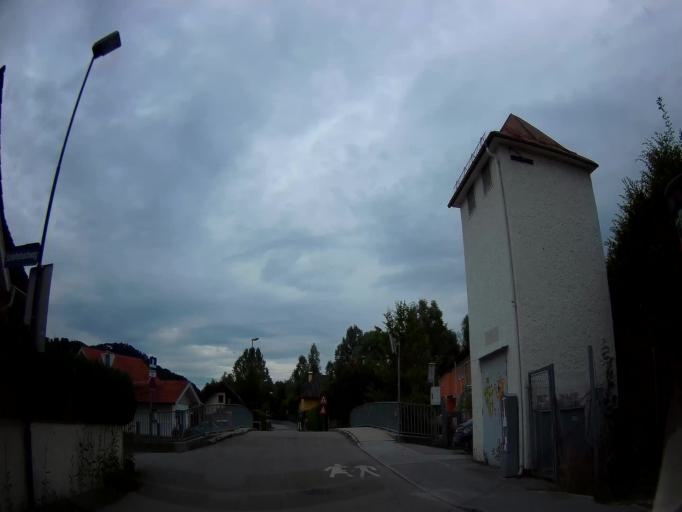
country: AT
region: Salzburg
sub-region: Politischer Bezirk Salzburg-Umgebung
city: Hallwang
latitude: 47.8260
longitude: 13.0663
